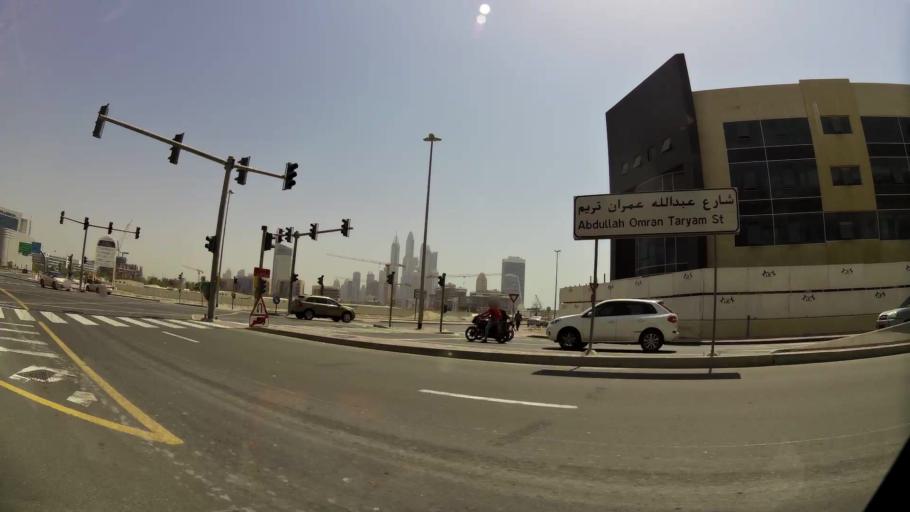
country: AE
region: Dubai
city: Dubai
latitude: 25.1029
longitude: 55.1672
